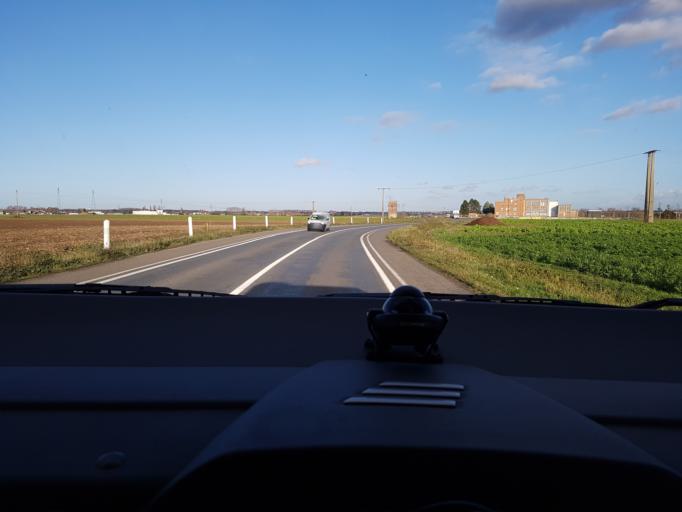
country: FR
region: Nord-Pas-de-Calais
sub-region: Departement du Nord
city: Camphin-en-Carembault
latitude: 50.5170
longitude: 2.9886
